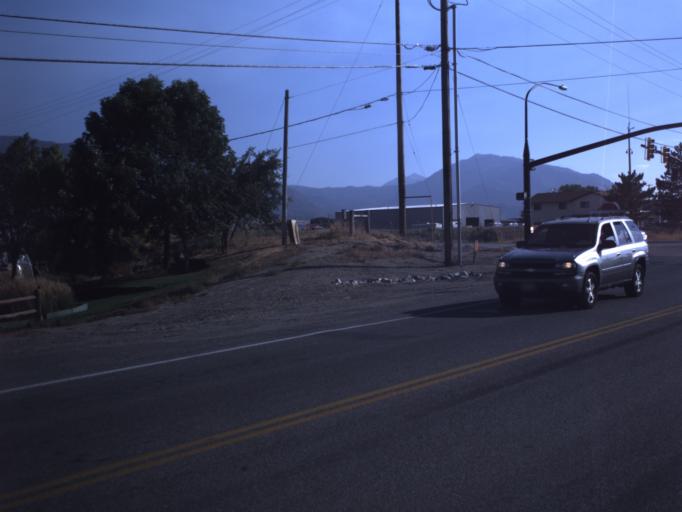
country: US
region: Utah
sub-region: Utah County
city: Spanish Fork
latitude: 40.0907
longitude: -111.6615
